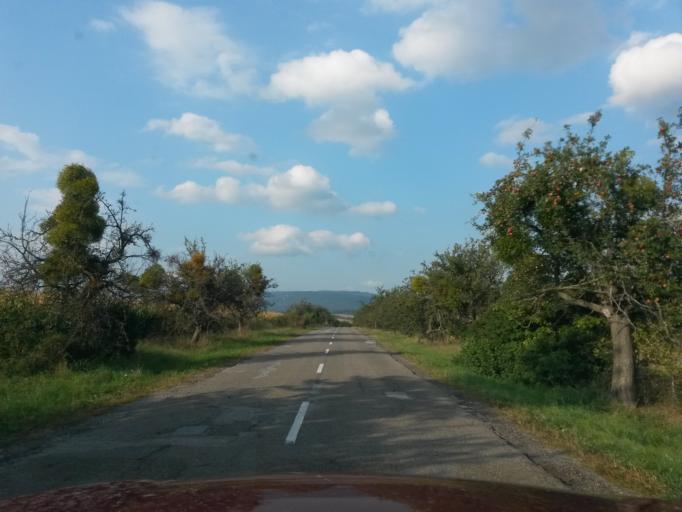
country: SK
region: Kosicky
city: Secovce
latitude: 48.7628
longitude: 21.4663
